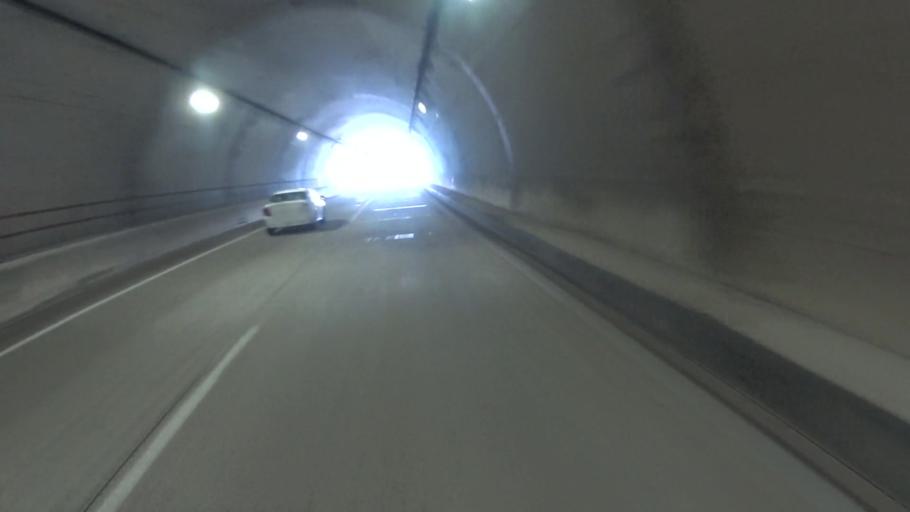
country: JP
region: Kyoto
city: Kameoka
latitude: 35.0695
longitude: 135.5202
